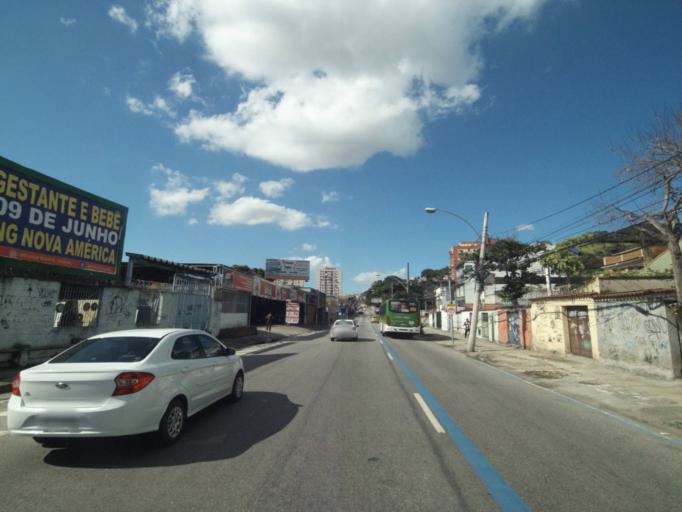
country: BR
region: Rio de Janeiro
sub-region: Rio De Janeiro
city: Rio de Janeiro
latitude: -22.9052
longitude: -43.2697
